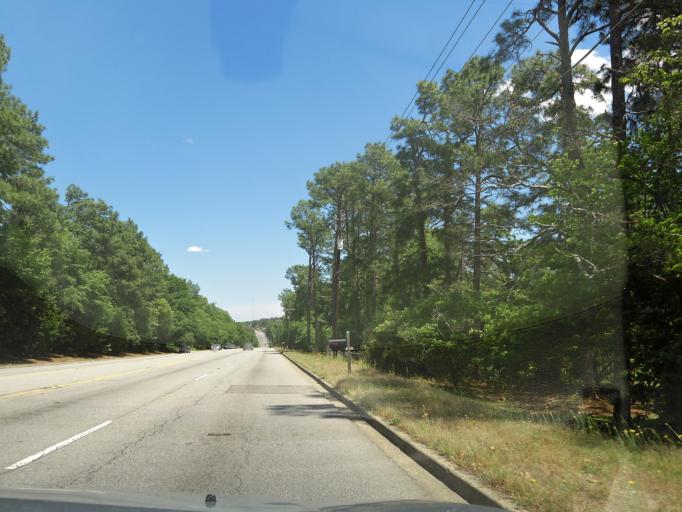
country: US
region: South Carolina
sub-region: Aiken County
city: Aiken
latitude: 33.5643
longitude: -81.7548
